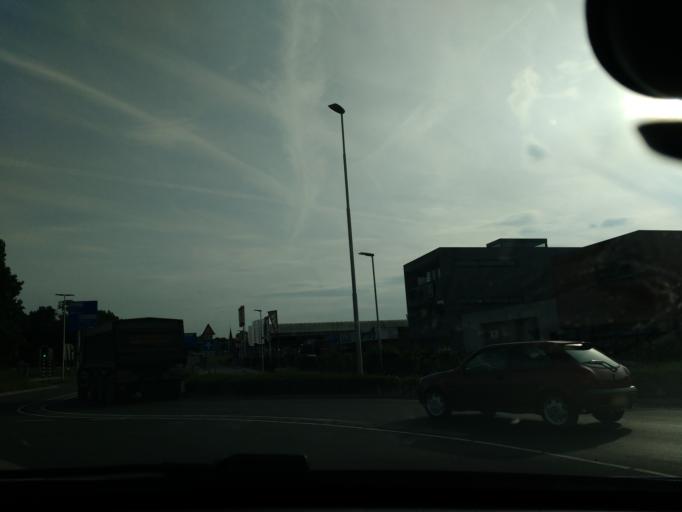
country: NL
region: Gelderland
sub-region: Gemeente Nijmegen
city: Lindenholt
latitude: 51.8385
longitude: 5.8176
